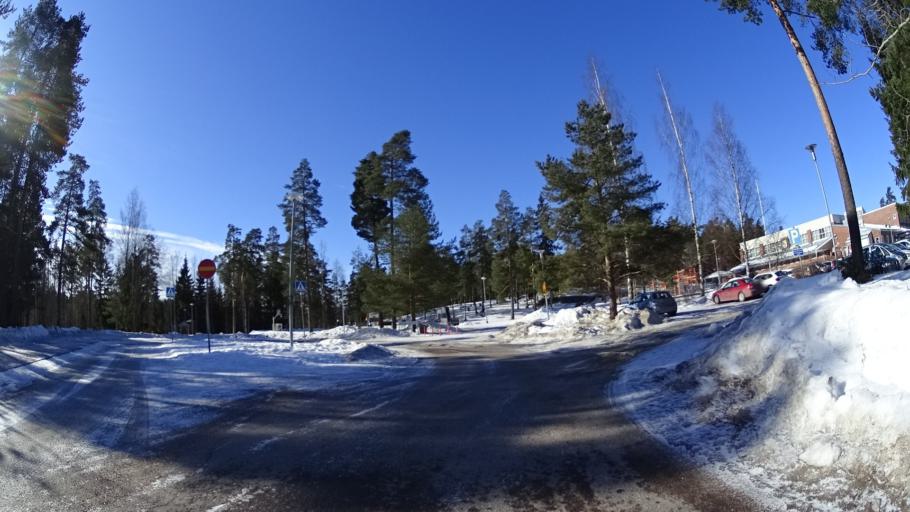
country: FI
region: Uusimaa
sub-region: Helsinki
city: Kauniainen
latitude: 60.1965
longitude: 24.7530
